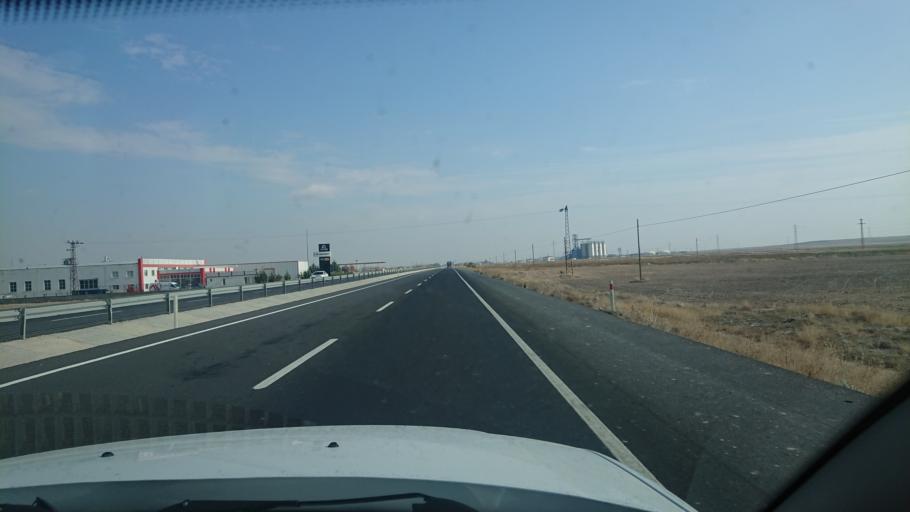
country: TR
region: Aksaray
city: Yesilova
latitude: 38.3194
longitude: 33.8628
